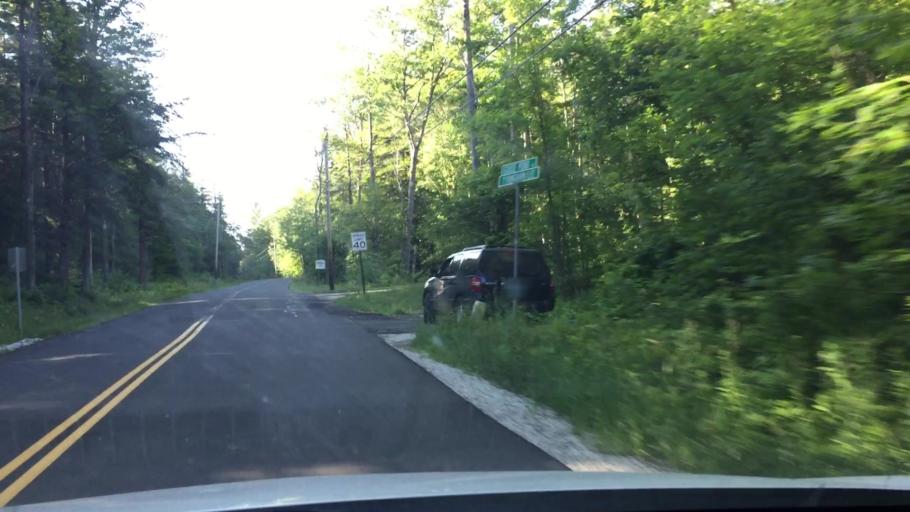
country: US
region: Massachusetts
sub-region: Berkshire County
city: Lee
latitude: 42.2804
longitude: -73.2101
